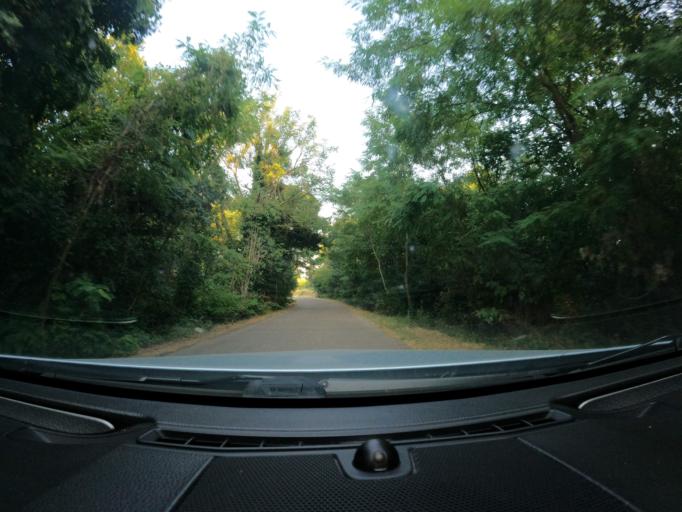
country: RS
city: Vrdnik
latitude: 45.1581
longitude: 19.7750
